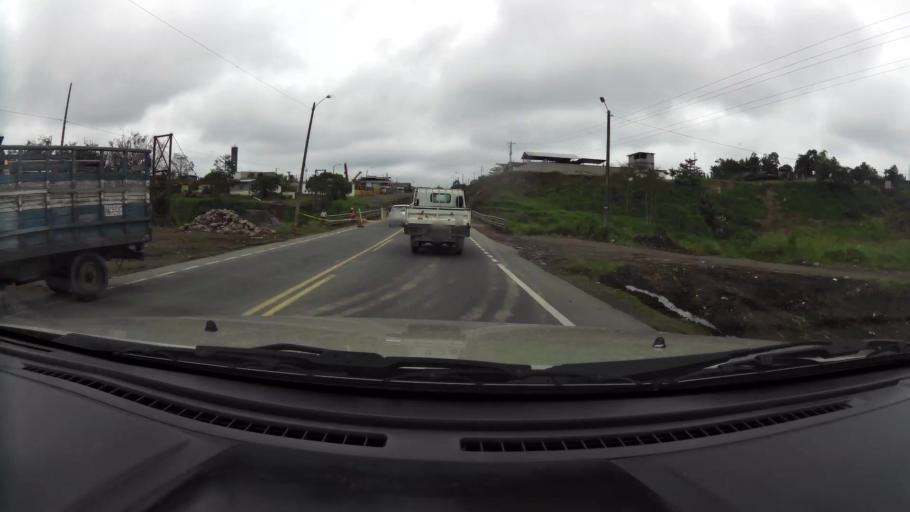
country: EC
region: Santo Domingo de los Tsachilas
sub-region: Canton Santo Domingo de los Colorados
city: Santo Domingo de los Colorados
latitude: -0.2794
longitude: -79.1776
